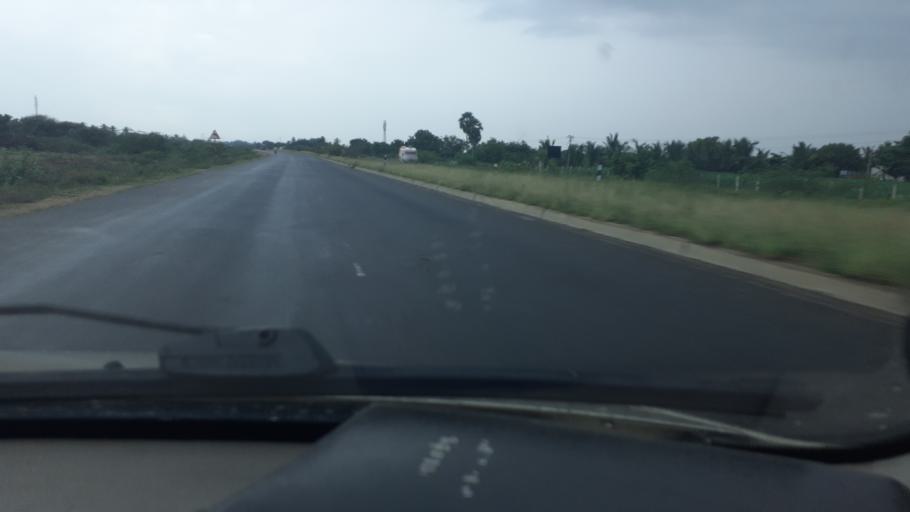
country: IN
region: Tamil Nadu
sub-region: Thoothukkudi
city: Kadambur
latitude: 9.0553
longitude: 77.7965
